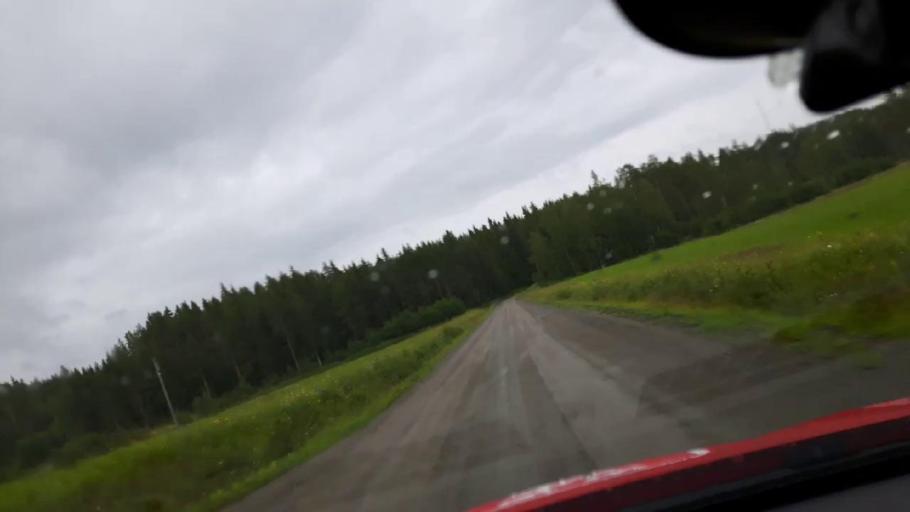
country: SE
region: Jaemtland
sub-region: OEstersunds Kommun
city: Brunflo
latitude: 62.9067
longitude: 14.8556
